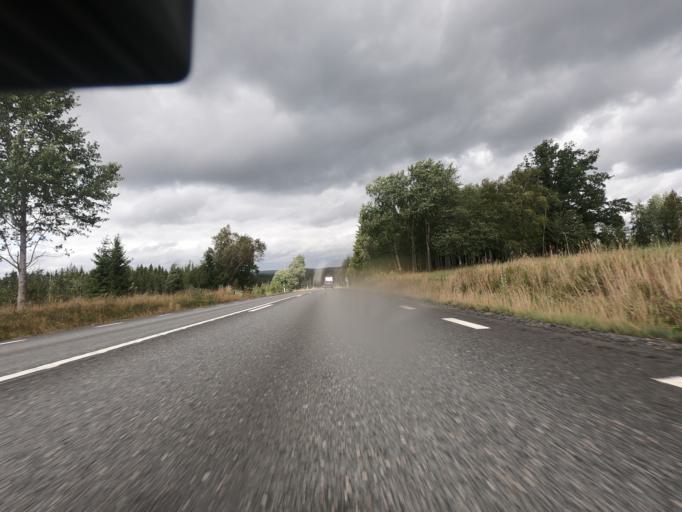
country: SE
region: Joenkoeping
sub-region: Savsjo Kommun
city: Vrigstad
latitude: 57.4214
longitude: 14.3308
